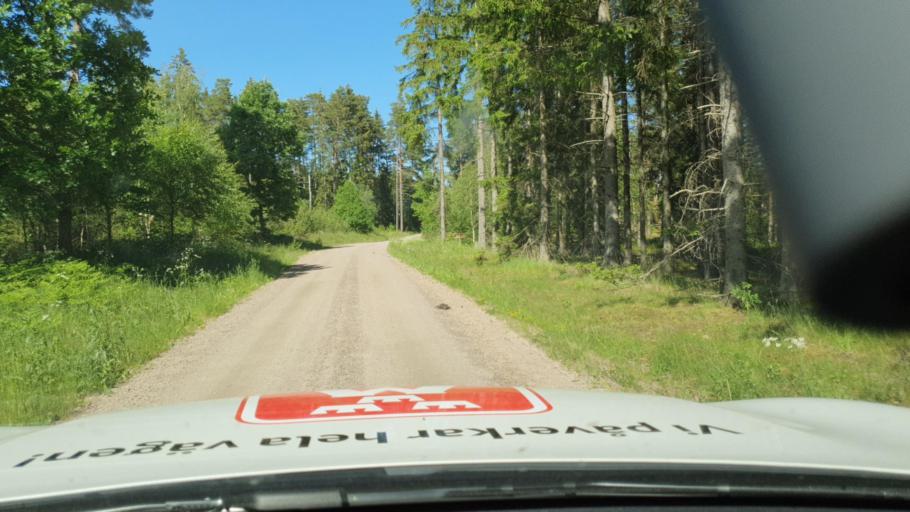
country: SE
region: Vaestra Goetaland
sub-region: Skovde Kommun
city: Skultorp
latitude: 58.3065
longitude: 13.8422
